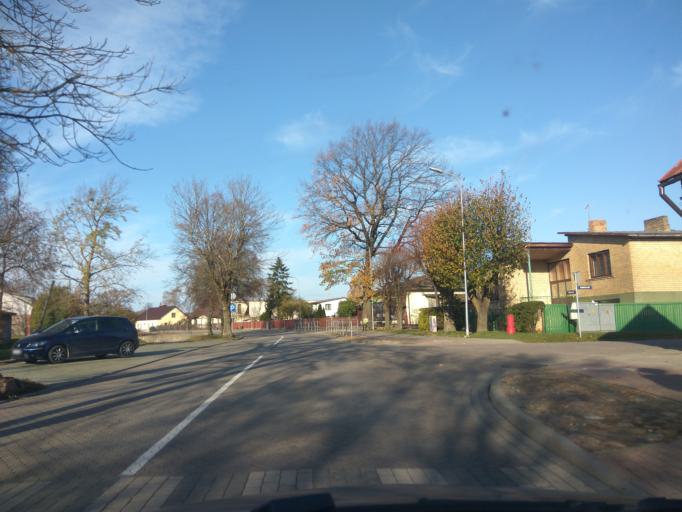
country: LV
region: Ventspils
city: Ventspils
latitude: 57.3777
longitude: 21.5733
